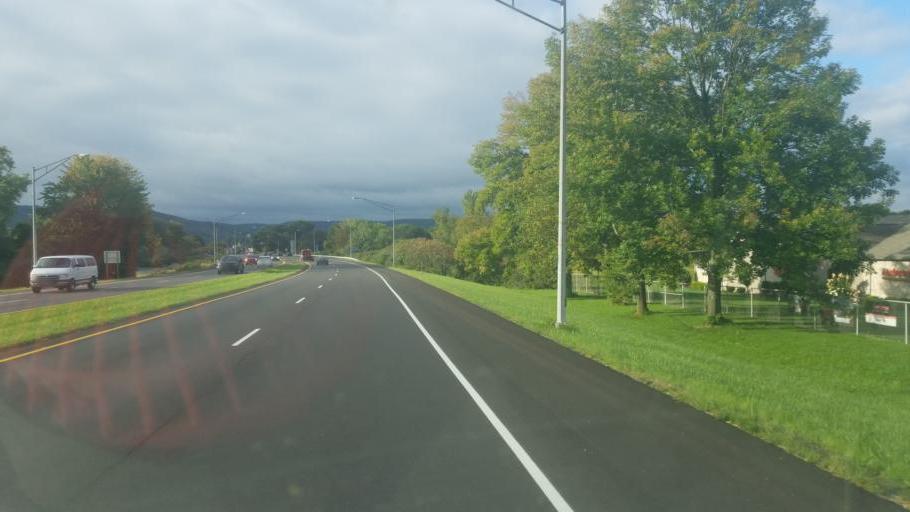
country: US
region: New York
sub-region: Cattaraugus County
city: Olean
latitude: 42.0923
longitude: -78.4290
